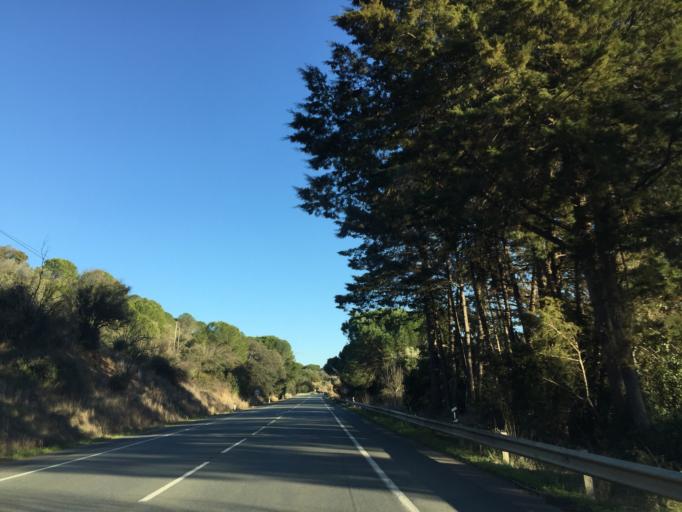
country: PT
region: Setubal
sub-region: Grandola
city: Grandola
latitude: 38.1256
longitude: -8.4595
